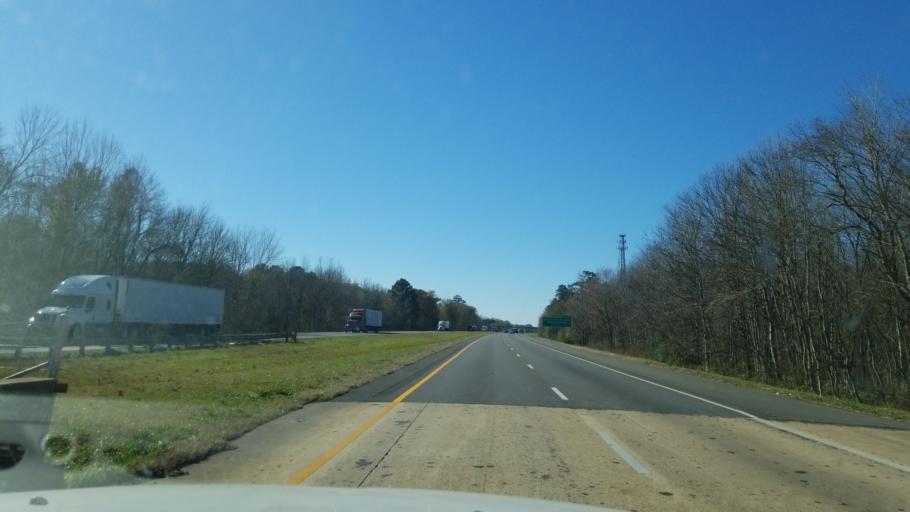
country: US
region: Alabama
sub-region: Tuscaloosa County
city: Tuscaloosa
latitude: 33.1588
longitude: -87.5788
